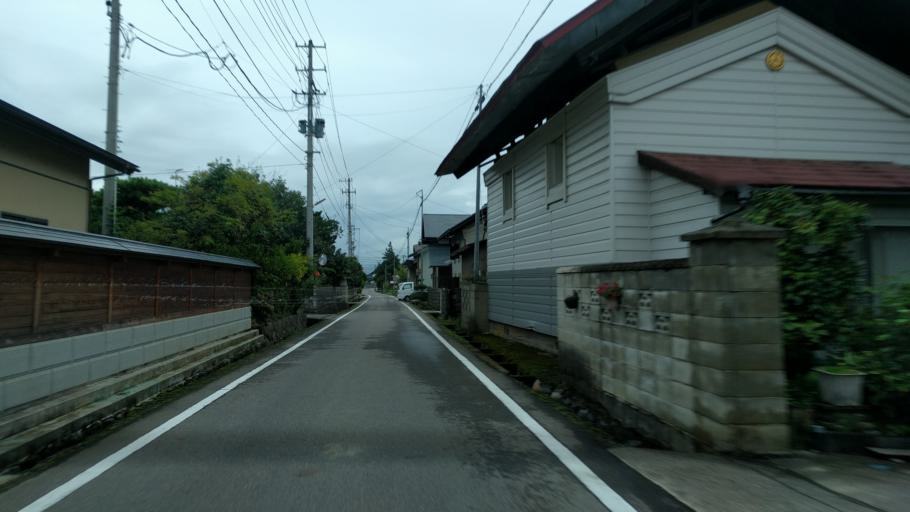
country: JP
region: Fukushima
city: Kitakata
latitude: 37.5875
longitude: 139.9087
